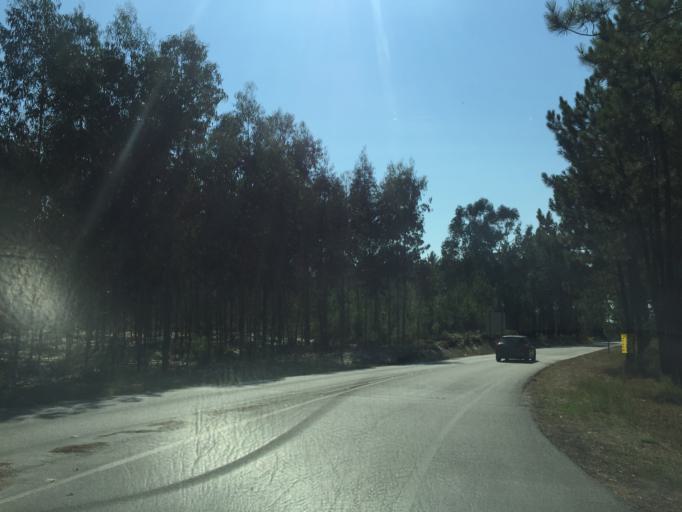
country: PT
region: Coimbra
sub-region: Montemor-O-Velho
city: Arazede
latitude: 40.3204
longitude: -8.6962
